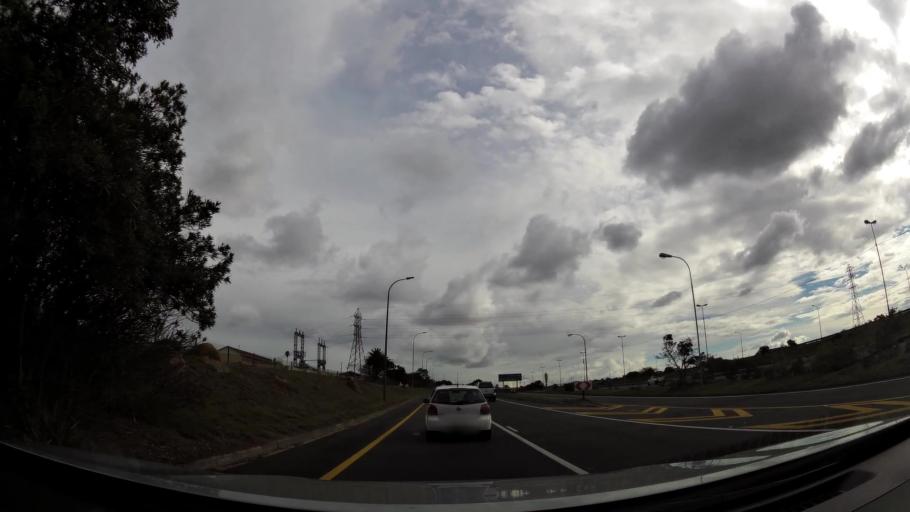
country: ZA
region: Eastern Cape
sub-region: Nelson Mandela Bay Metropolitan Municipality
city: Port Elizabeth
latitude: -33.9466
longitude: 25.5318
